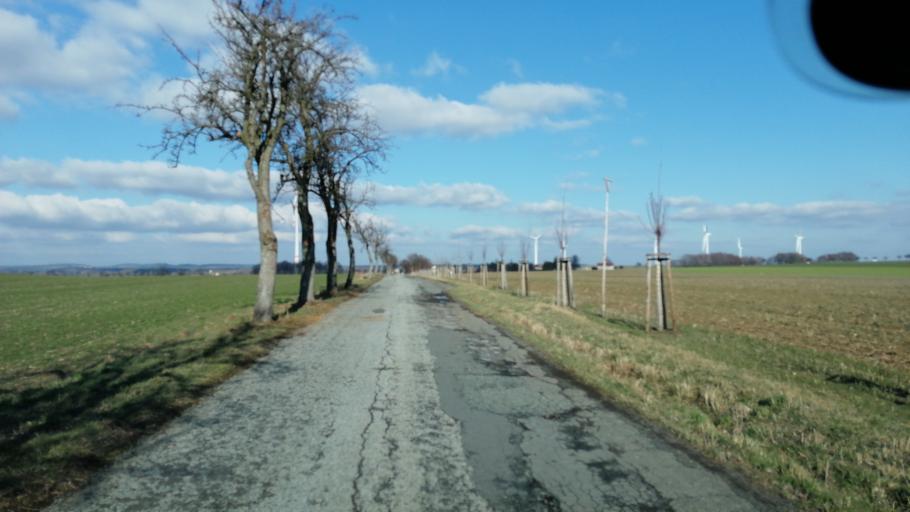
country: DE
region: Saxony
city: Weissenberg
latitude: 51.1703
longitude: 14.7102
